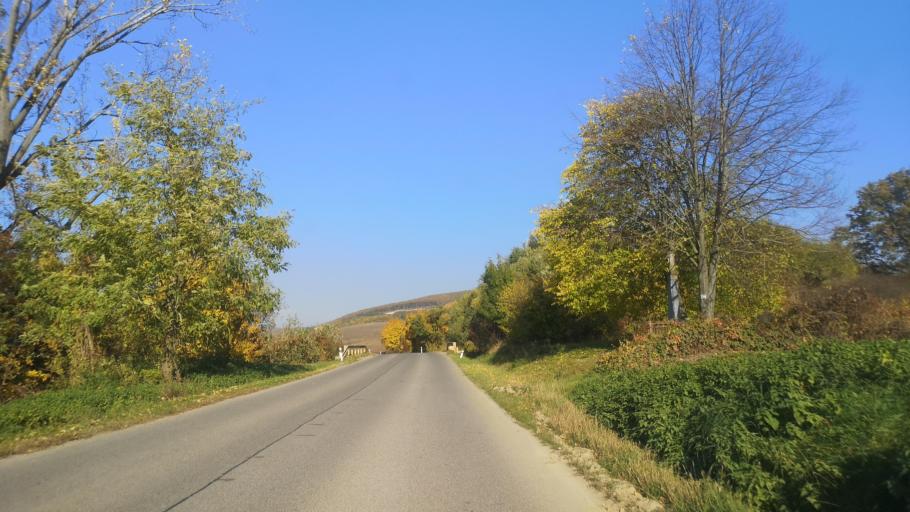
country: SK
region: Nitriansky
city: Zlate Moravce
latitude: 48.4325
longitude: 18.4289
